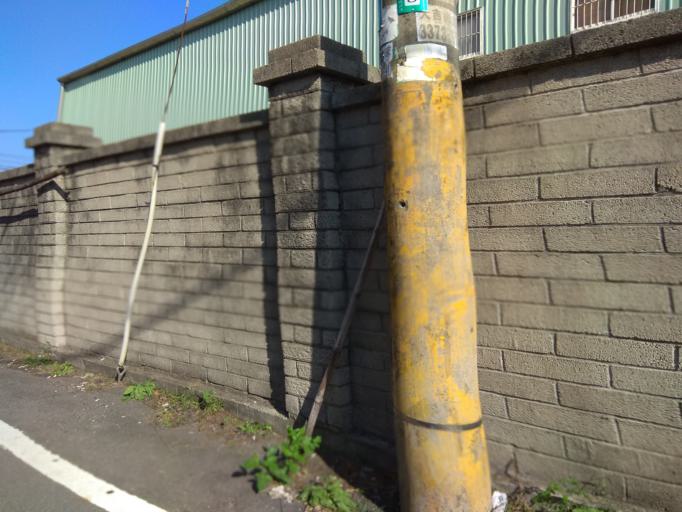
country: TW
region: Taiwan
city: Taoyuan City
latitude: 25.0546
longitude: 121.2208
